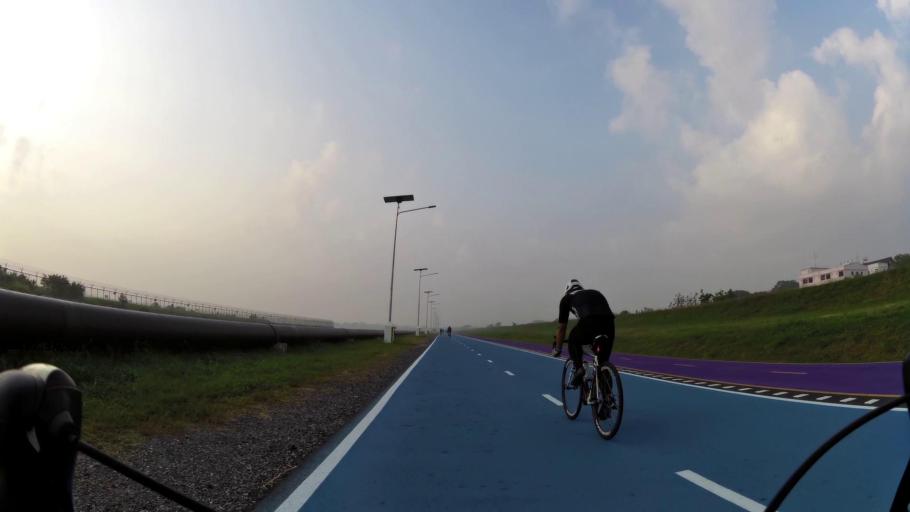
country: TH
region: Bangkok
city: Lat Krabang
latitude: 13.6894
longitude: 100.7709
